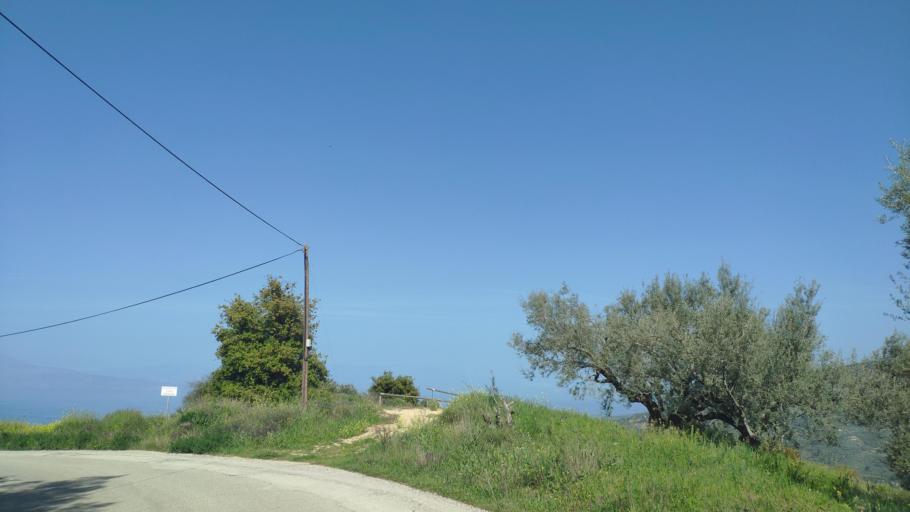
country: GR
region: West Greece
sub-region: Nomos Achaias
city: Aiyira
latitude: 38.1159
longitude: 22.3332
